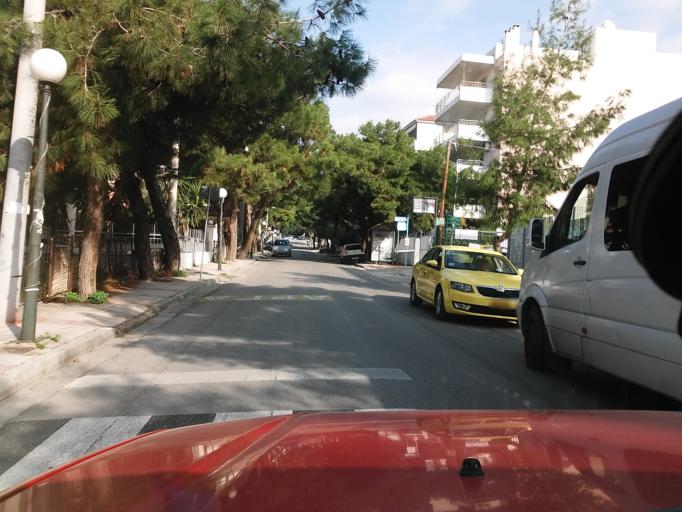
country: GR
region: Attica
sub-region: Nomarchia Athinas
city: Irakleio
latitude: 38.0547
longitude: 23.7718
